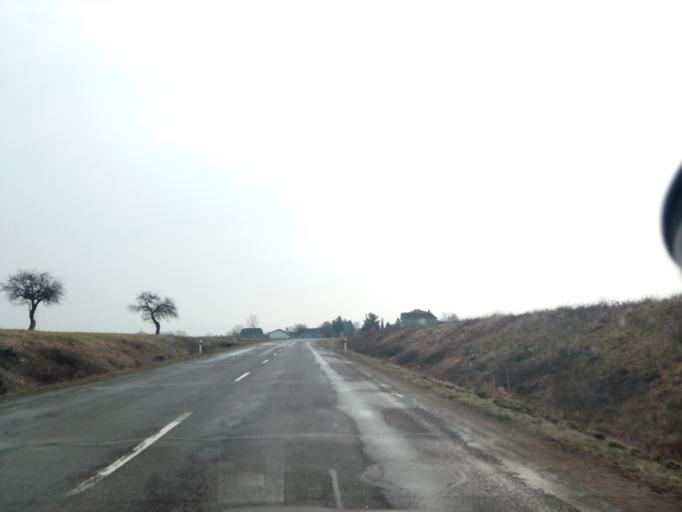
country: SK
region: Kosicky
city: Secovce
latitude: 48.6191
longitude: 21.5953
